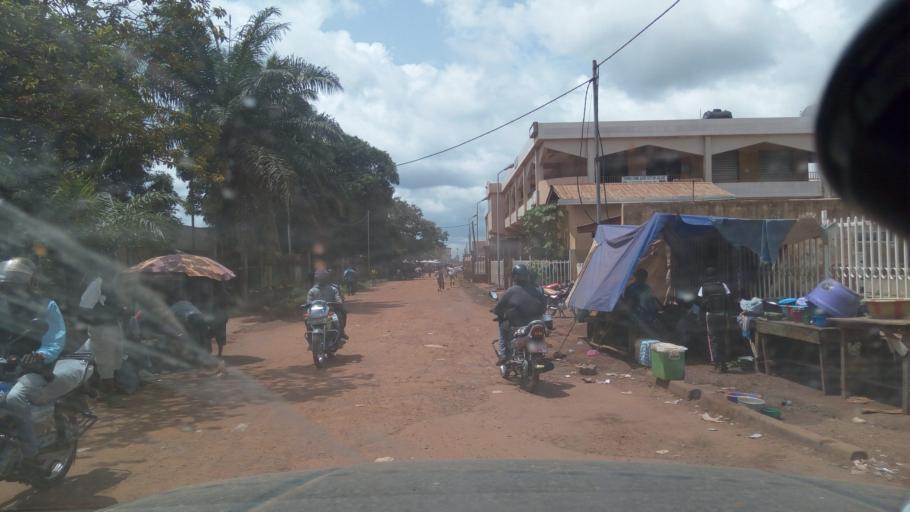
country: SL
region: Eastern Province
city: Kenema
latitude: 7.8802
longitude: -11.1903
